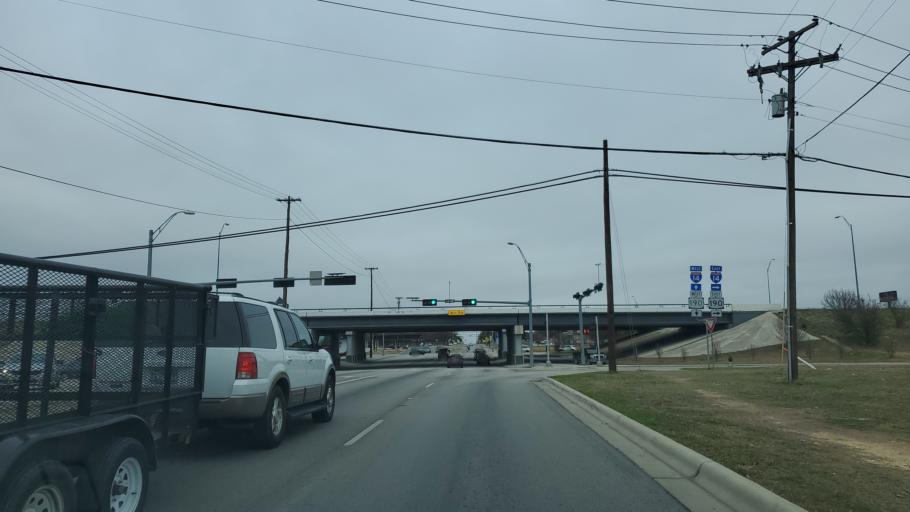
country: US
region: Texas
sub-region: Bell County
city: Killeen
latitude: 31.0937
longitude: -97.7327
